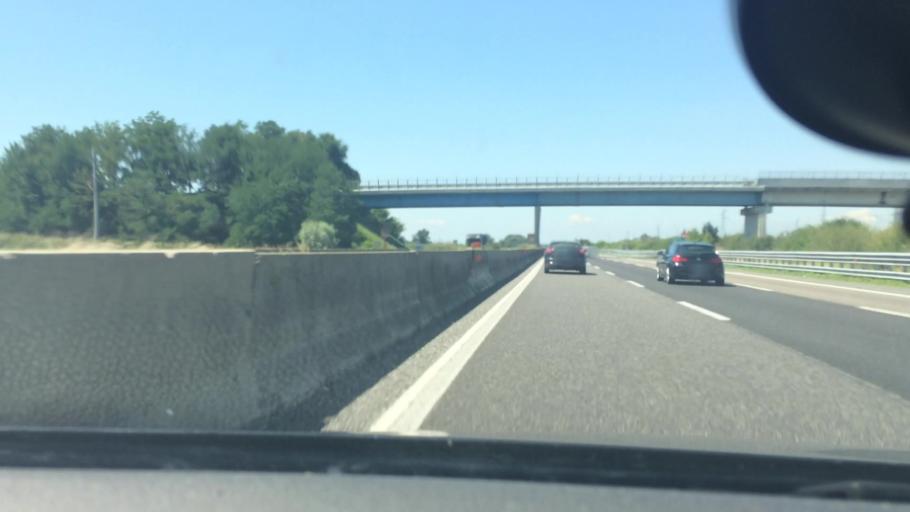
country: IT
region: Lombardy
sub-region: Provincia di Lodi
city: Villanova del Sillaro
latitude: 45.2457
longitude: 9.4900
